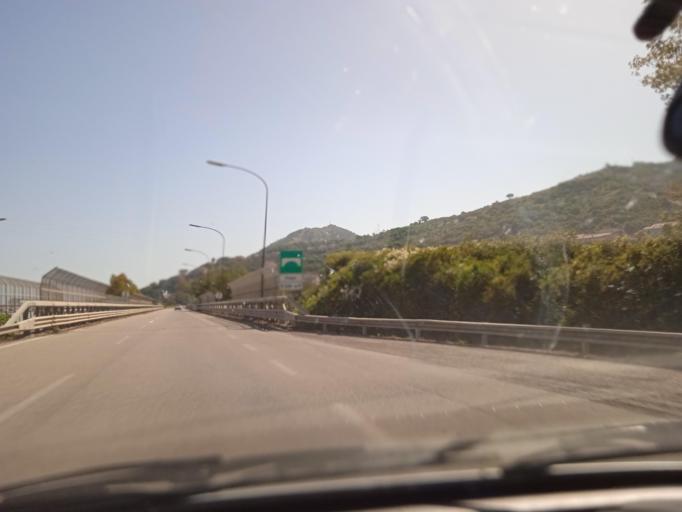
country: IT
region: Sicily
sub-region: Messina
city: Brolo
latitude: 38.1489
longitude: 14.8295
